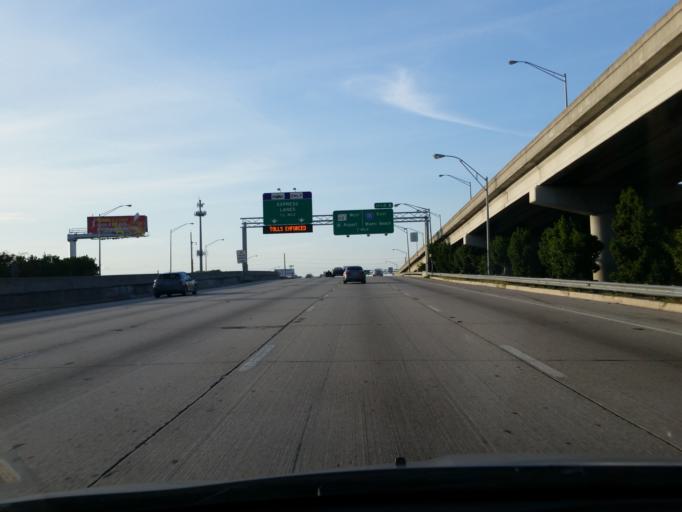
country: US
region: Florida
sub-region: Miami-Dade County
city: Miami
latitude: 25.7938
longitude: -80.2052
